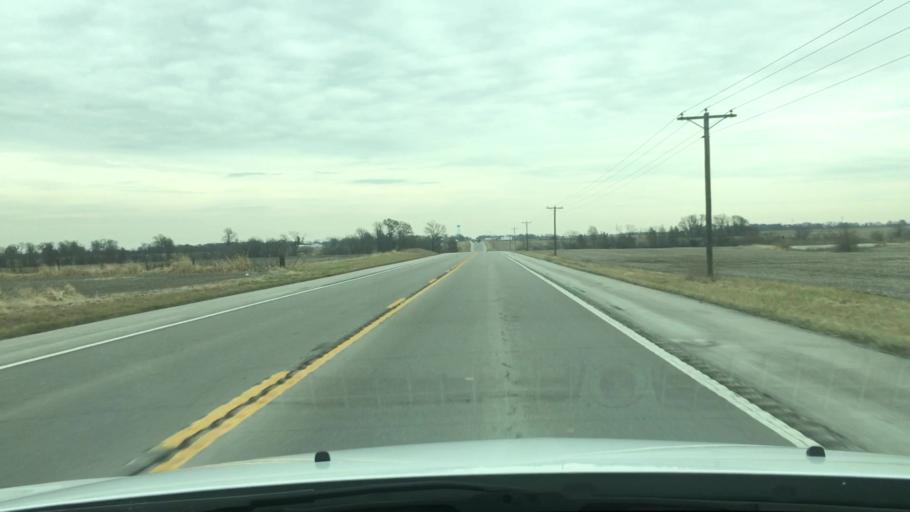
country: US
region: Missouri
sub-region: Montgomery County
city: Wellsville
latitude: 39.1633
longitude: -91.6673
